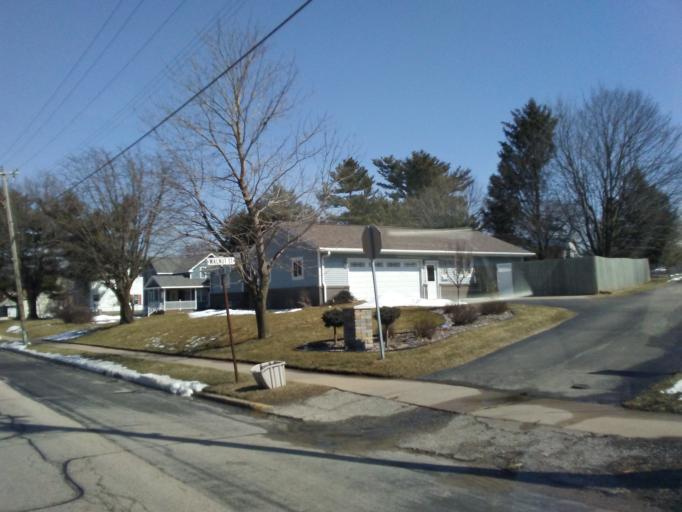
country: US
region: Wisconsin
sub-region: Vernon County
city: Westby
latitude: 43.6473
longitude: -90.8613
